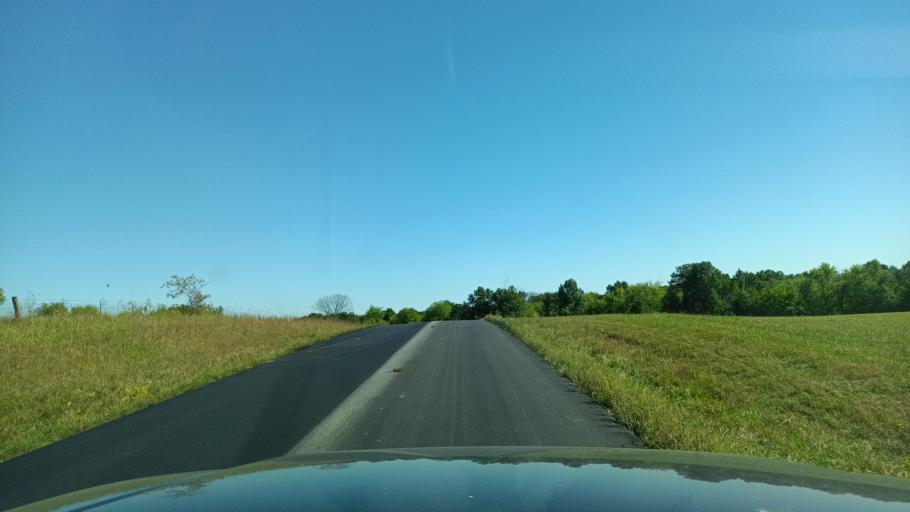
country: US
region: Missouri
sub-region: Macon County
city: La Plata
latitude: 39.9214
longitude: -92.5315
